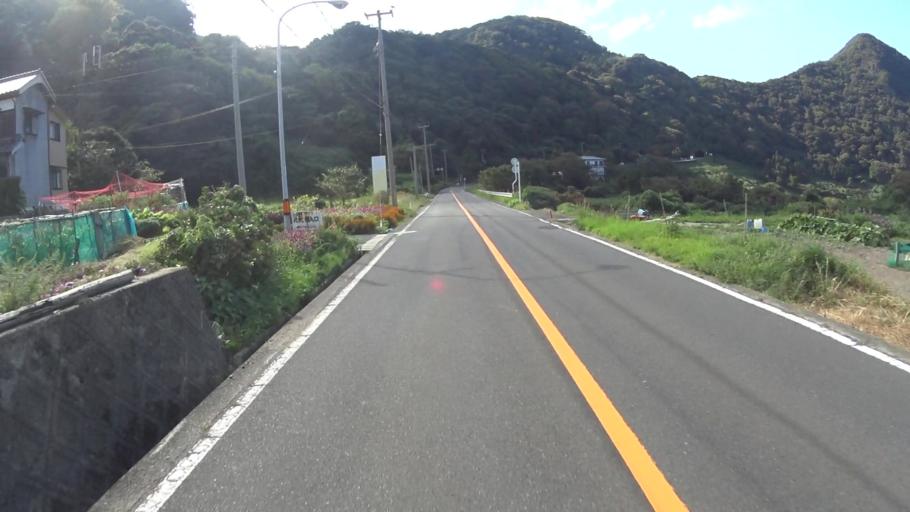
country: JP
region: Kyoto
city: Miyazu
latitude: 35.7488
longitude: 135.1431
